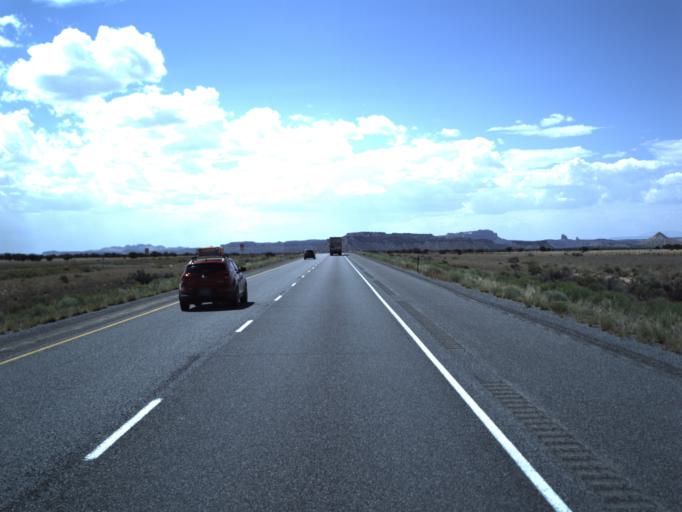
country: US
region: Utah
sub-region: Emery County
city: Castle Dale
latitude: 38.8965
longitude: -110.6047
